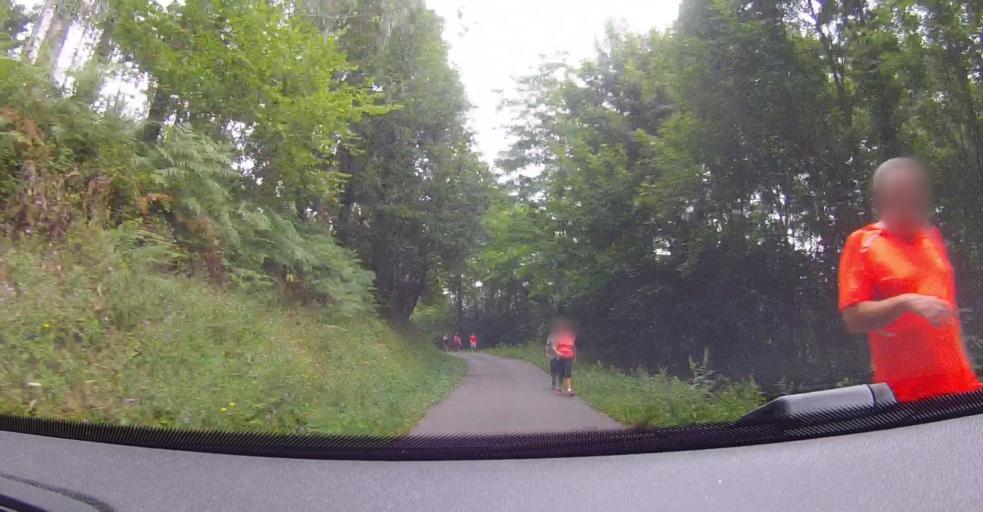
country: ES
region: Basque Country
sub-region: Bizkaia
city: Sopuerta
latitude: 43.2584
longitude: -3.1470
